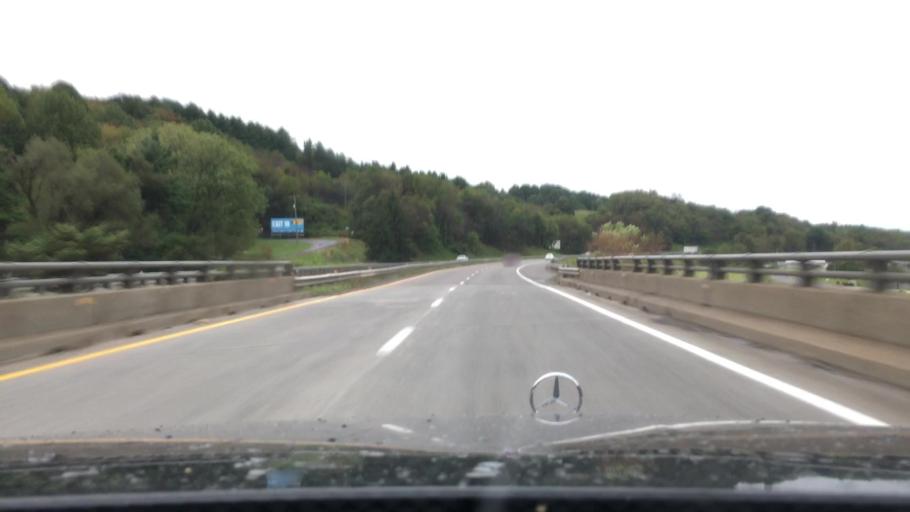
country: US
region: Virginia
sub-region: Smyth County
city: Atkins
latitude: 36.8747
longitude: -81.3989
